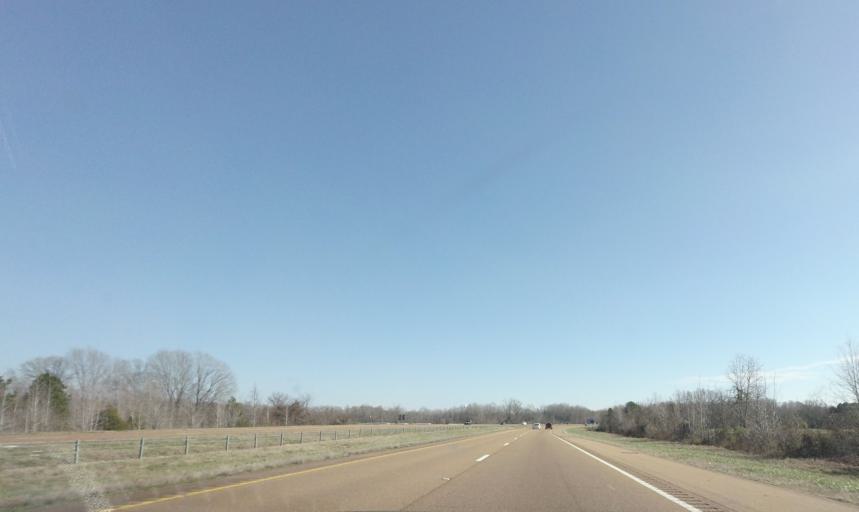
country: US
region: Mississippi
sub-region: Union County
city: New Albany
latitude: 34.5185
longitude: -89.0589
